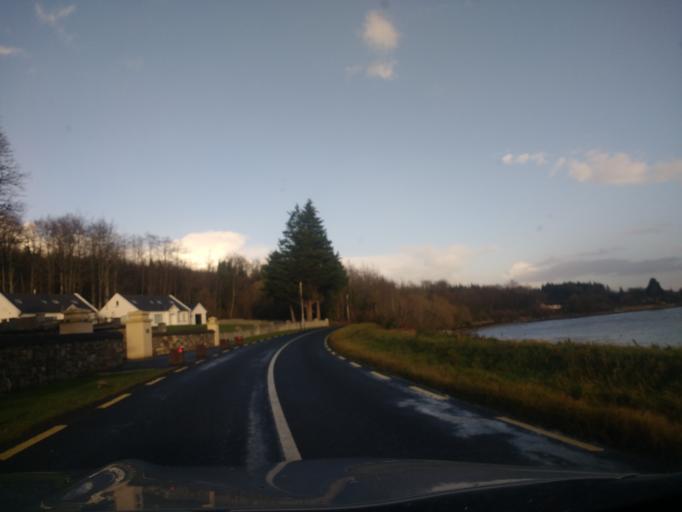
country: IE
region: Ulster
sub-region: County Donegal
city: Ramelton
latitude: 55.0807
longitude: -7.5874
